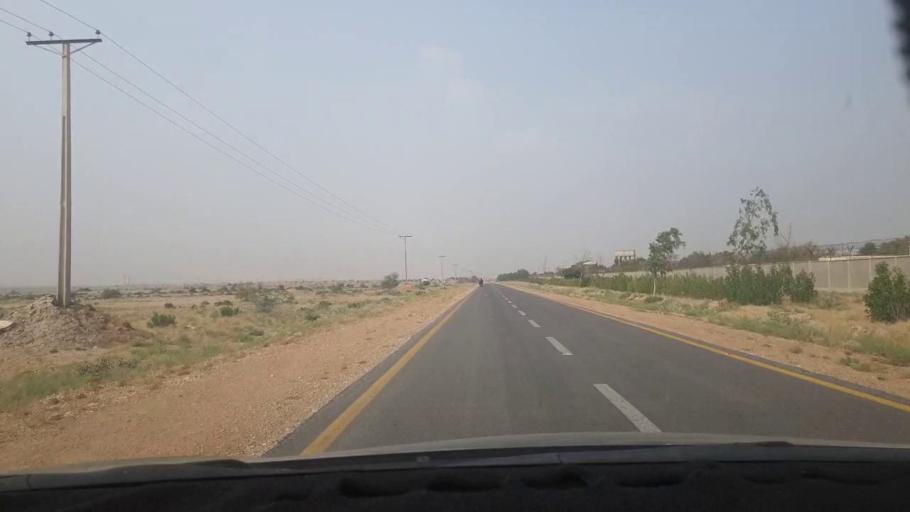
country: PK
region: Sindh
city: Jamshoro
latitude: 25.5561
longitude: 68.3197
